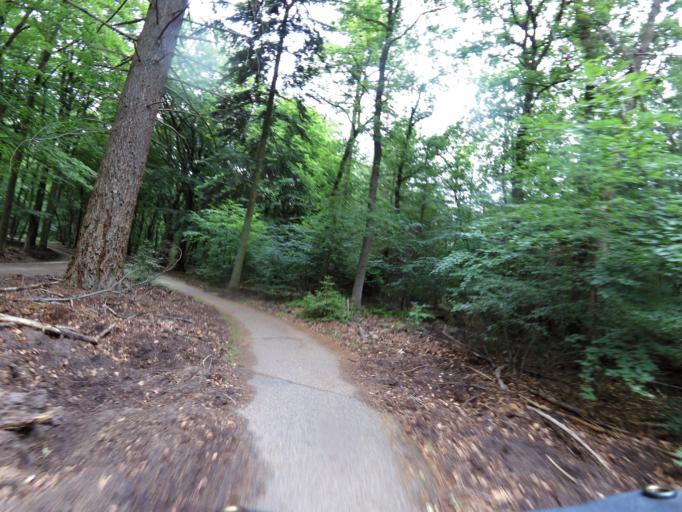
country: NL
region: Gelderland
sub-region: Gemeente Apeldoorn
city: Uddel
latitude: 52.2872
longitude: 5.8044
